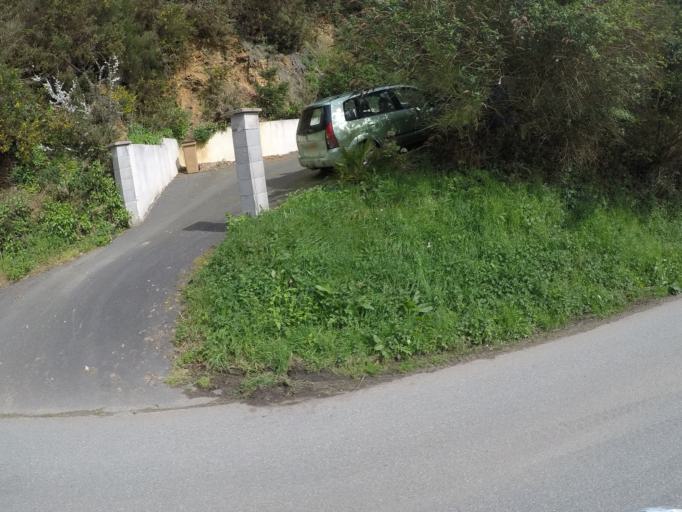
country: FR
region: Brittany
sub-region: Departement des Cotes-d'Armor
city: Plouezec
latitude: 48.7299
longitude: -2.9510
